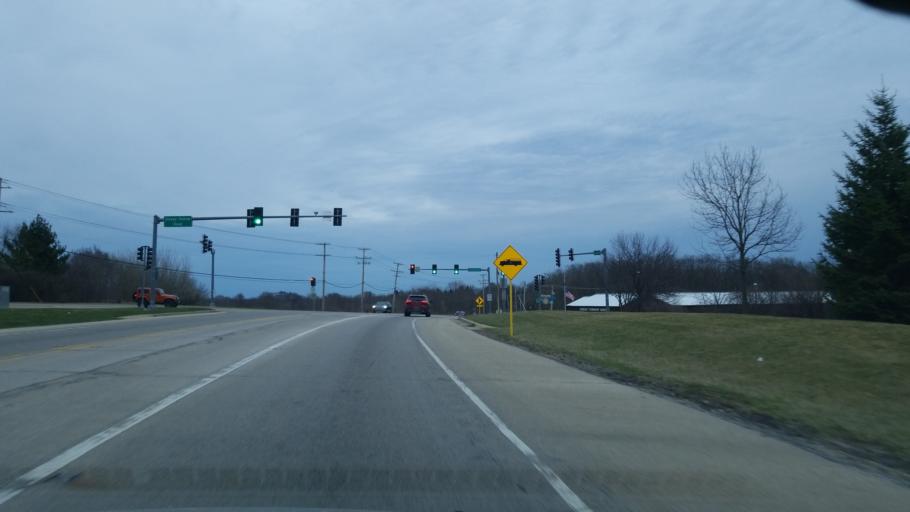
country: US
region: Illinois
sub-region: Kane County
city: Sleepy Hollow
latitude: 42.1029
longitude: -88.3165
